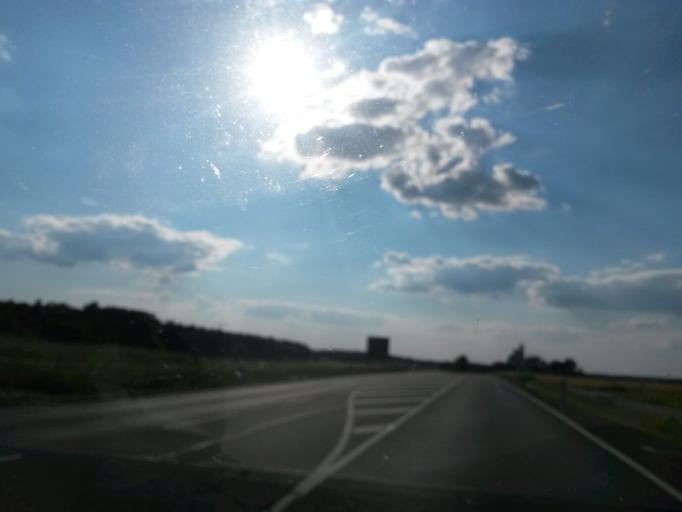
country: DE
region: Bavaria
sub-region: Regierungsbezirk Mittelfranken
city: Emskirchen
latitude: 49.5661
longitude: 10.6803
